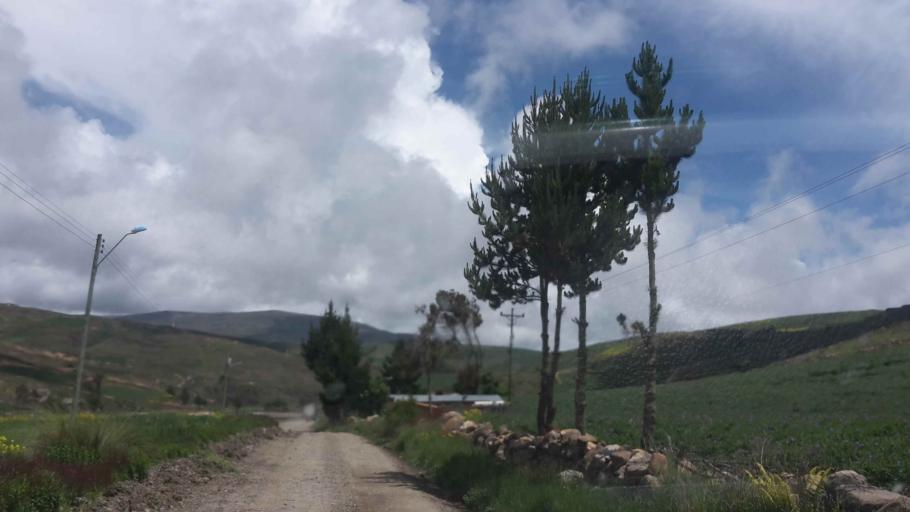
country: BO
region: Cochabamba
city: Cochabamba
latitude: -17.2143
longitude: -66.0846
